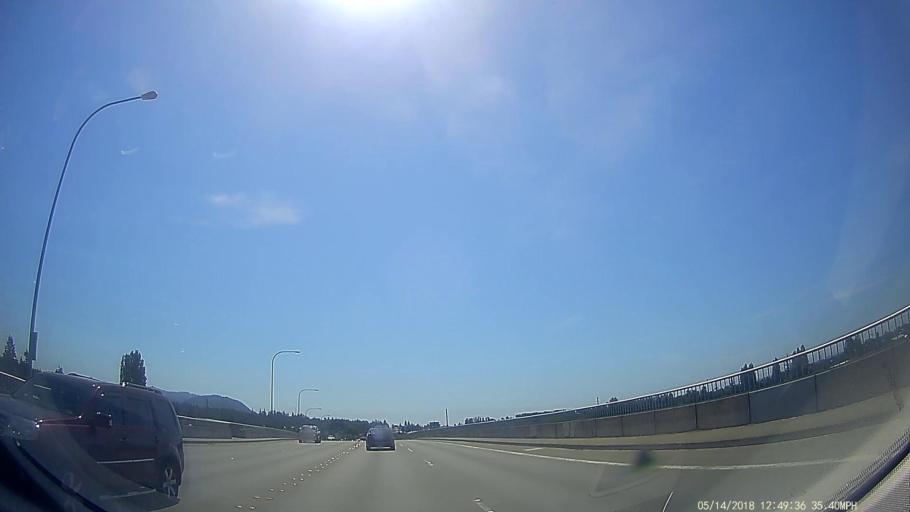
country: US
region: Washington
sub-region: Skagit County
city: Mount Vernon
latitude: 48.4452
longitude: -122.3357
